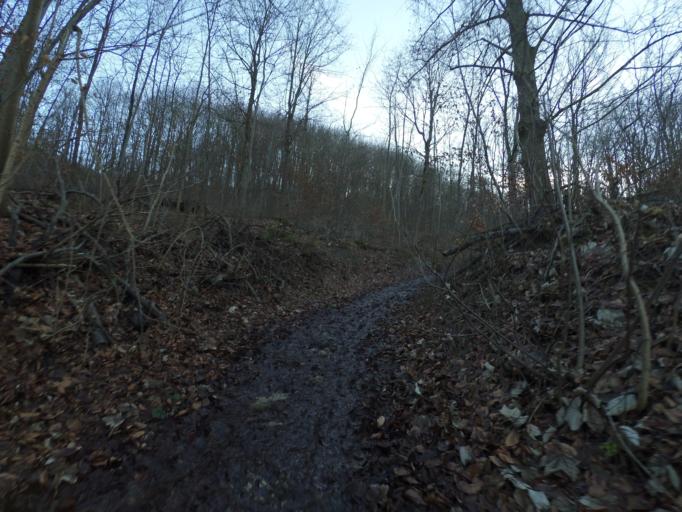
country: DE
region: Baden-Wuerttemberg
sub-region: Regierungsbezirk Stuttgart
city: Aalen
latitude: 48.8224
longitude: 10.1017
